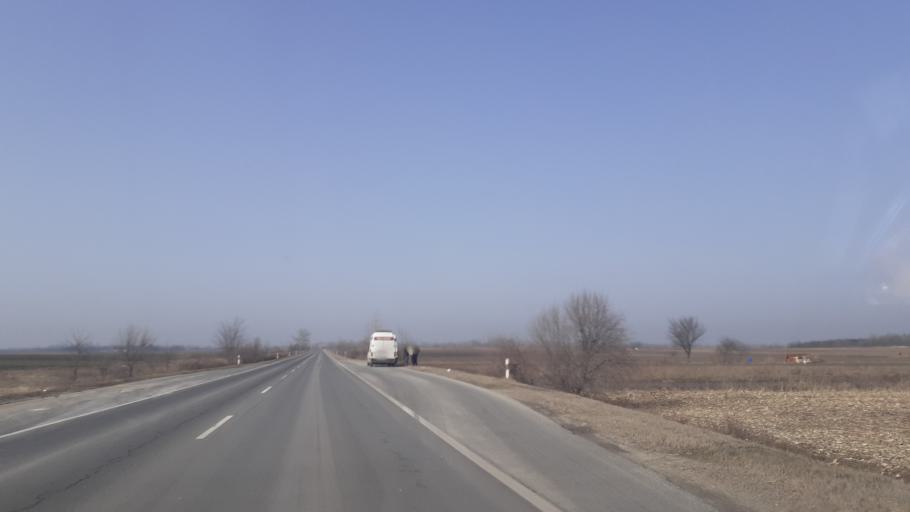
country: HU
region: Pest
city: Bugyi
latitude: 47.2243
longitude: 19.1257
